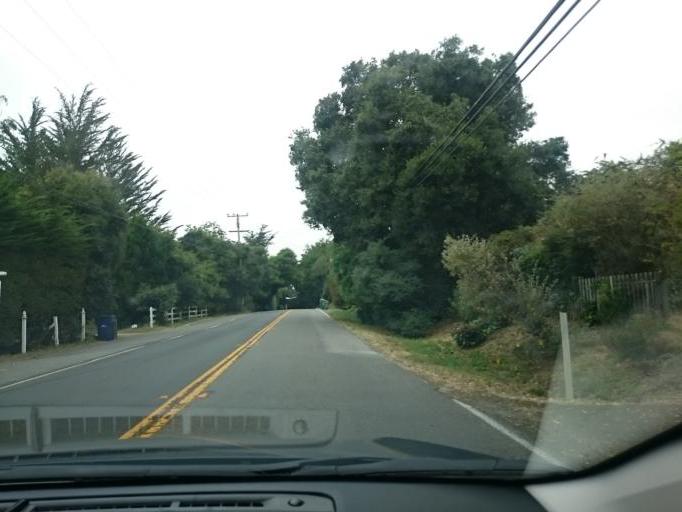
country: US
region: California
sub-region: Marin County
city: Inverness
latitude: 38.0738
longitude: -122.8016
